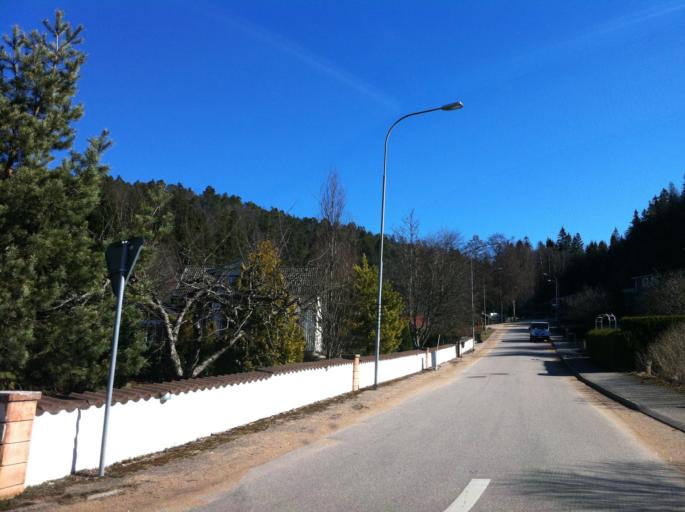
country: SE
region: Vaestra Goetaland
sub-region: Vanersborgs Kommun
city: Vargon
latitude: 58.3523
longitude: 12.4079
